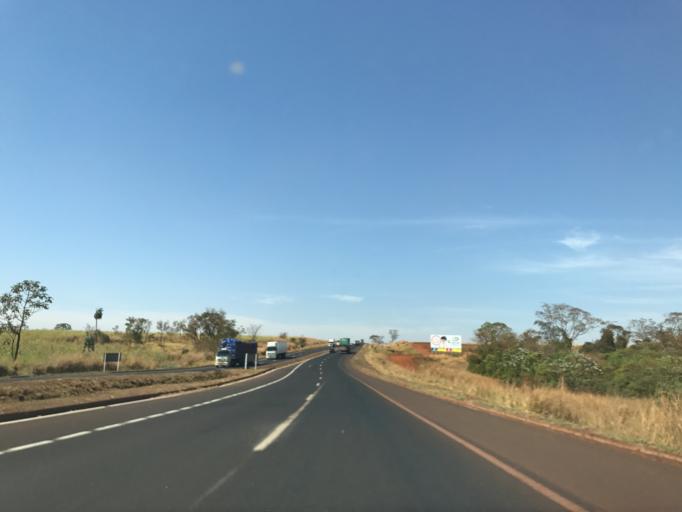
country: BR
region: Minas Gerais
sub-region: Centralina
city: Centralina
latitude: -18.5447
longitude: -49.1941
